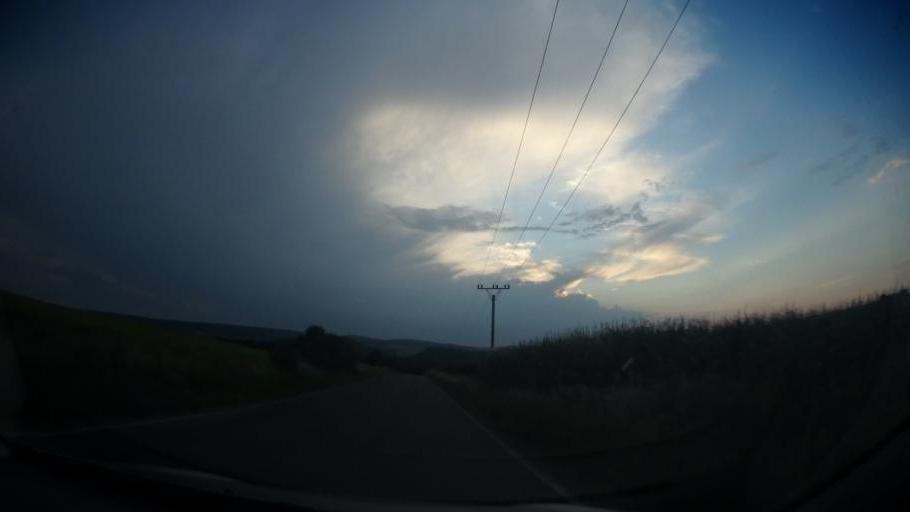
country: CZ
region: South Moravian
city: Dolni Kounice
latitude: 49.0700
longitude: 16.4827
